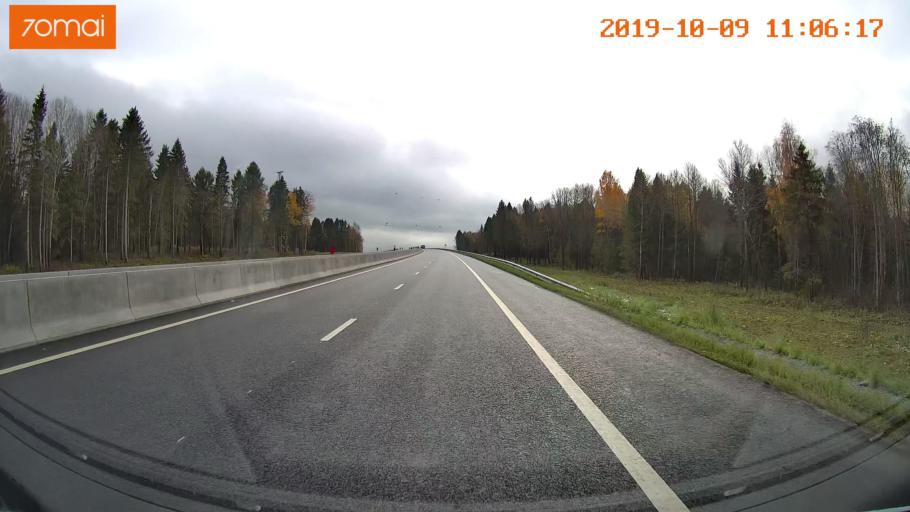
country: RU
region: Vologda
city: Vologda
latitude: 59.1886
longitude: 39.7594
